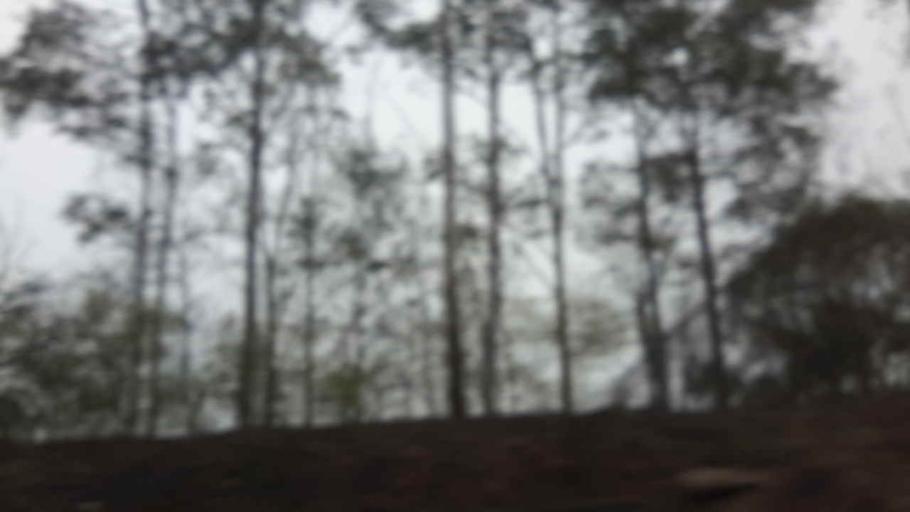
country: AU
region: New South Wales
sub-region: Penrith Municipality
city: Cambridge Park
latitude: -33.7498
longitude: 150.7135
